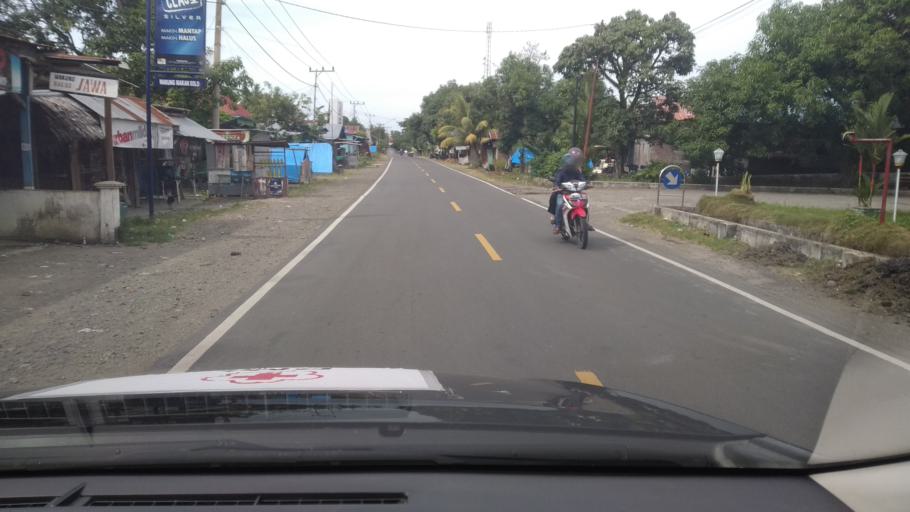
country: ID
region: Sulawesi Barat
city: Malunda
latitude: -3.0068
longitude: 118.8565
